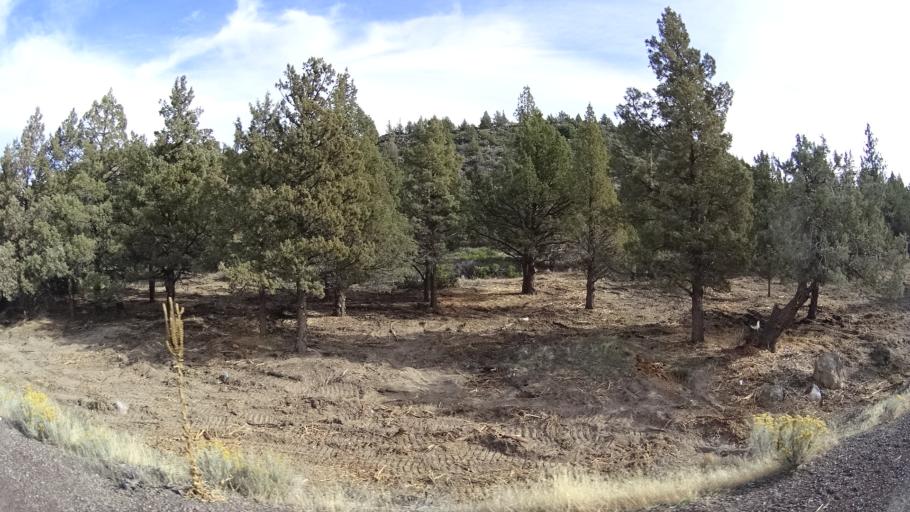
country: US
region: California
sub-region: Siskiyou County
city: Weed
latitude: 41.5207
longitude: -122.3663
